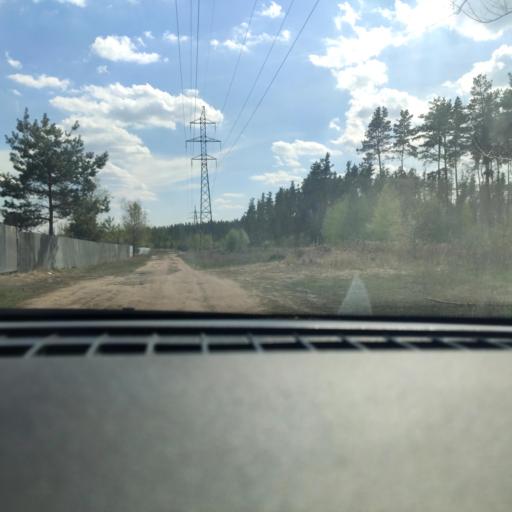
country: RU
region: Voronezj
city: Maslovka
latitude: 51.5949
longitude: 39.2158
